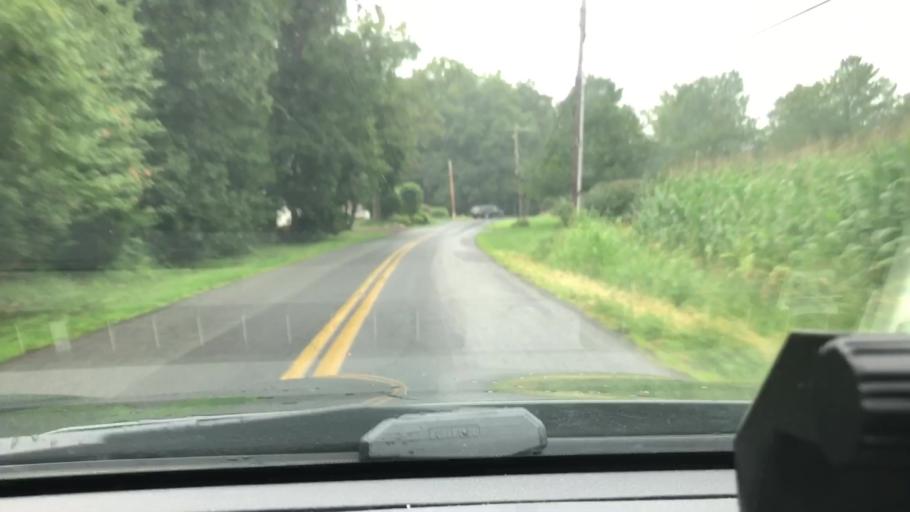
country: US
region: Pennsylvania
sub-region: Bucks County
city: Spinnerstown
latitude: 40.4403
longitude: -75.4358
